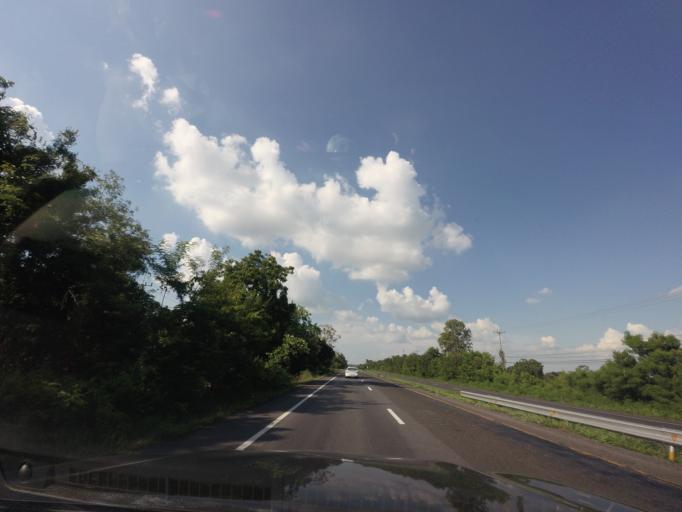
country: TH
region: Nakhon Ratchasima
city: Bua Lai
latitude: 15.6716
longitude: 102.5753
